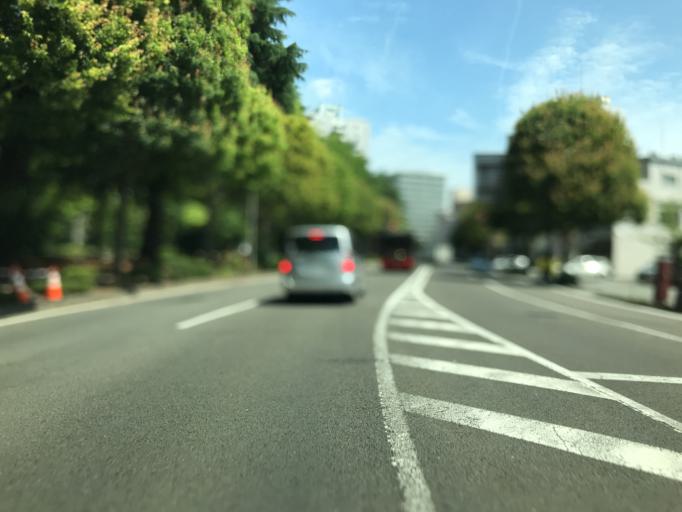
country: JP
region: Miyagi
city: Sendai
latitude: 38.2627
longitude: 140.8628
